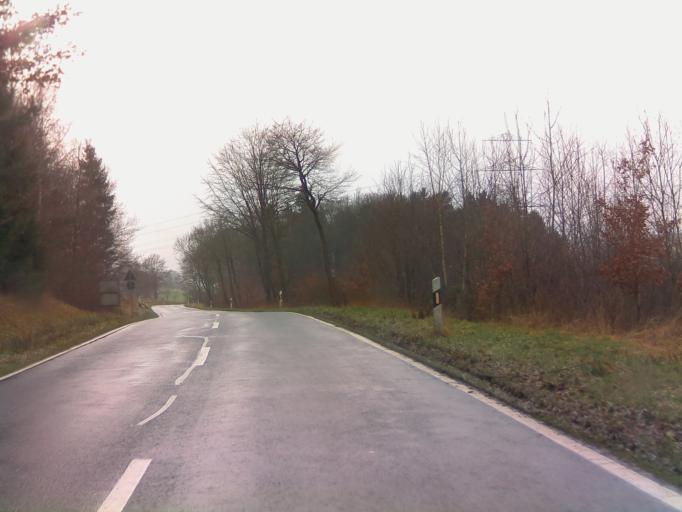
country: DE
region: Hesse
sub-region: Regierungsbezirk Kassel
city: Neuhof
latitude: 50.4621
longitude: 9.6468
